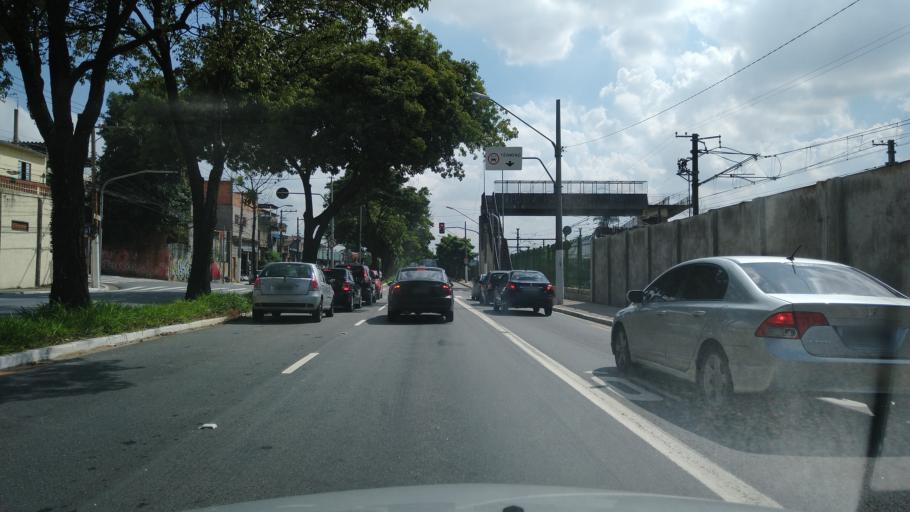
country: BR
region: Sao Paulo
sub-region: Guarulhos
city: Guarulhos
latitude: -23.5093
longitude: -46.5468
